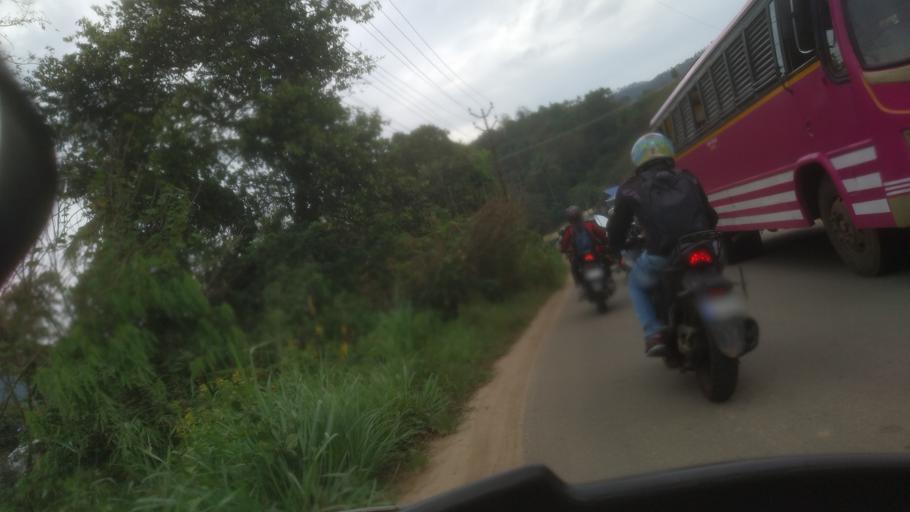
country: IN
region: Kerala
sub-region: Idukki
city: Munnar
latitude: 10.0069
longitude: 76.9630
